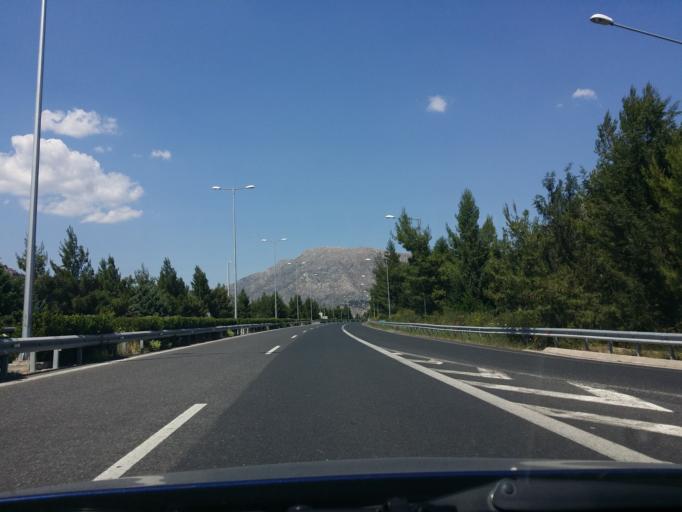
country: GR
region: Peloponnese
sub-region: Nomos Arkadias
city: Tripoli
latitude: 37.5901
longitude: 22.4363
